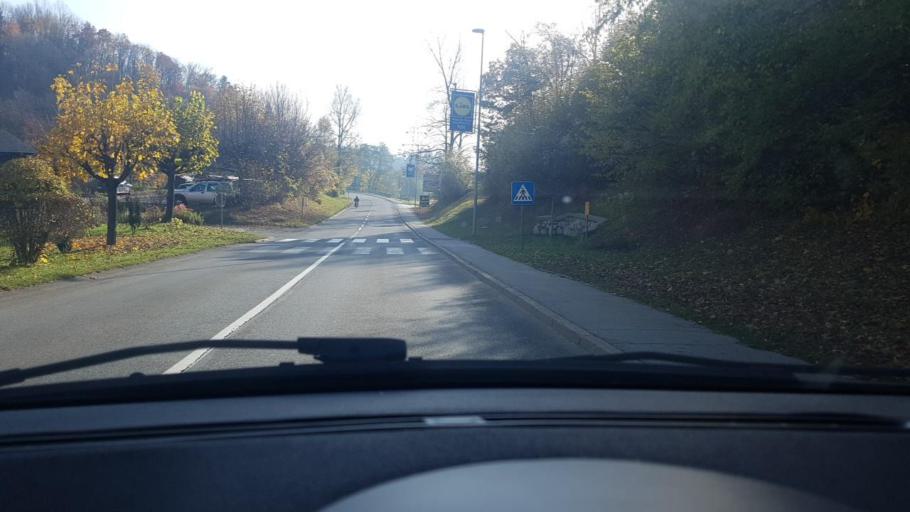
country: SI
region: Trzic
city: Bistrica pri Trzicu
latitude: 46.3556
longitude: 14.2962
